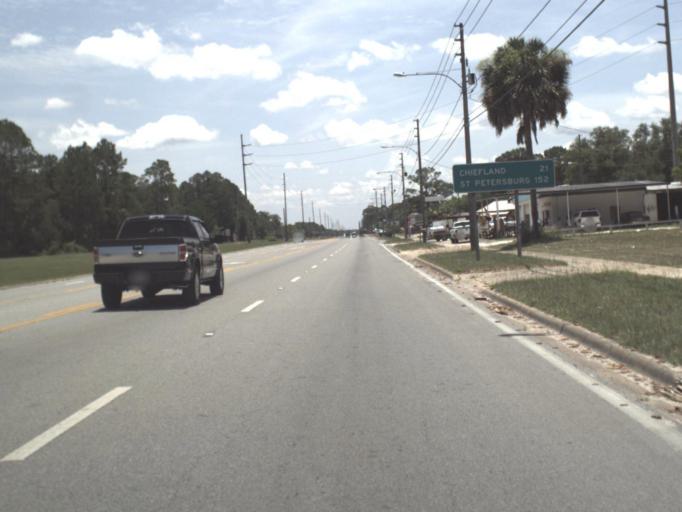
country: US
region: Florida
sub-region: Dixie County
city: Cross City
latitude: 29.6325
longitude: -83.1217
